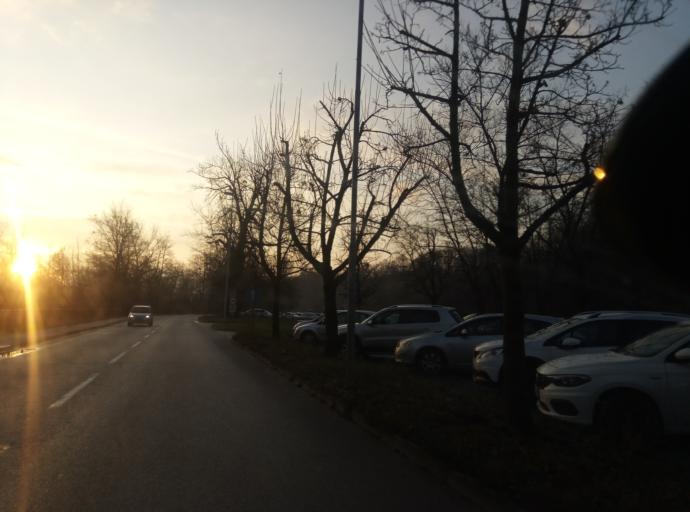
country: SI
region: Kranj
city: Kranj
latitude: 46.2339
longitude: 14.3546
